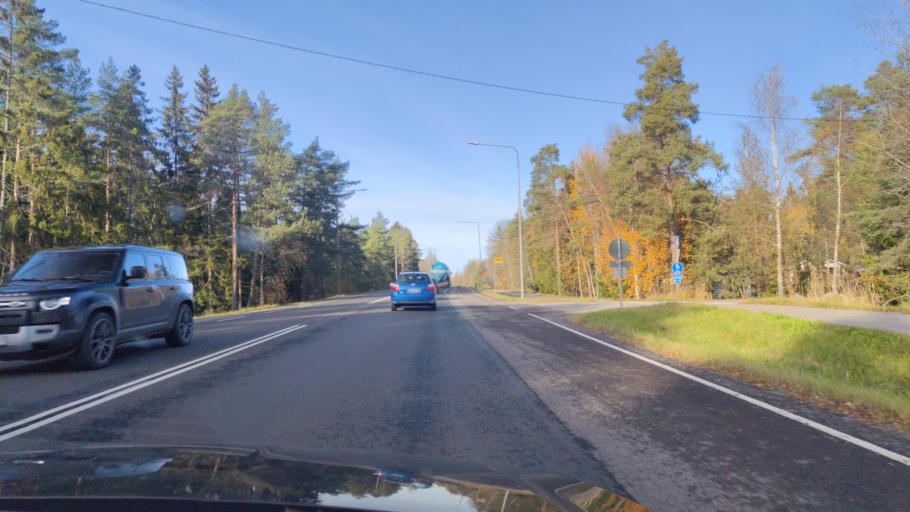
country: FI
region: Varsinais-Suomi
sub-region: Turku
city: Kaarina
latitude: 60.4481
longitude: 22.3737
